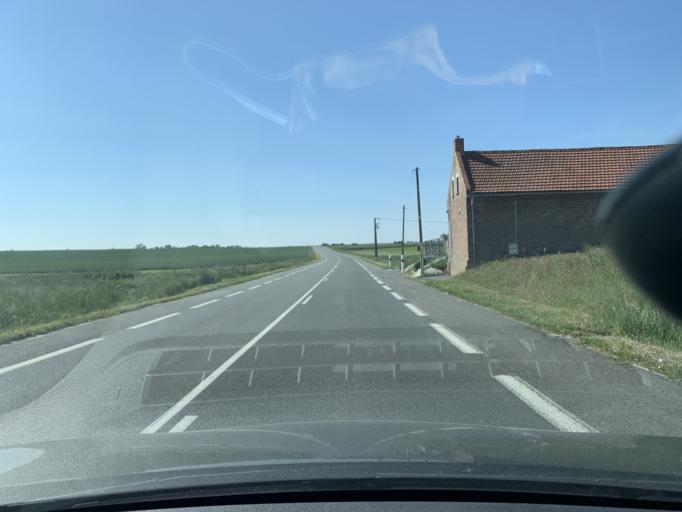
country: FR
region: Nord-Pas-de-Calais
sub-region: Departement du Nord
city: Cambrai
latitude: 50.1476
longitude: 3.2430
